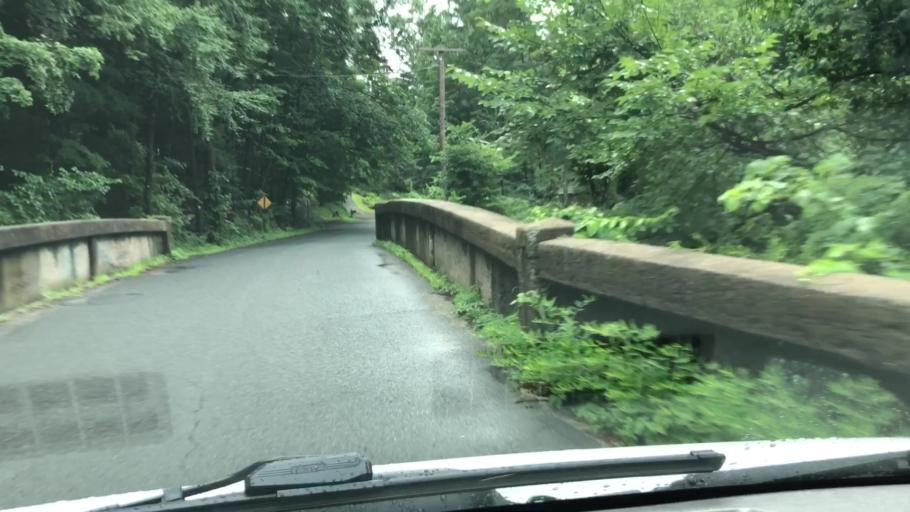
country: US
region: Massachusetts
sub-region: Hampshire County
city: Williamsburg
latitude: 42.3690
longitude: -72.7015
